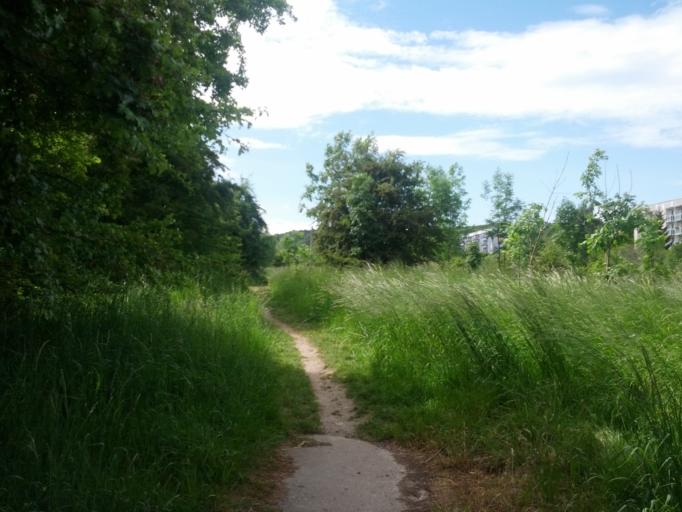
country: DE
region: Thuringia
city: Eisenach
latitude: 50.9926
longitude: 10.3079
